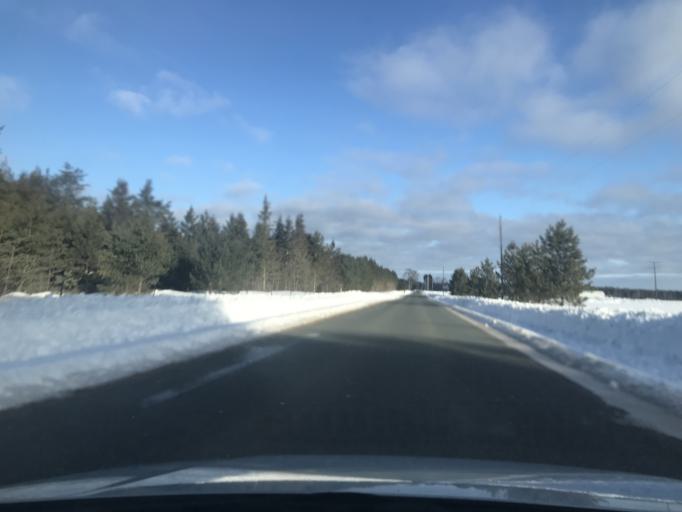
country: US
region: Wisconsin
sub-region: Marinette County
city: Niagara
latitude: 45.6121
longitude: -87.9770
